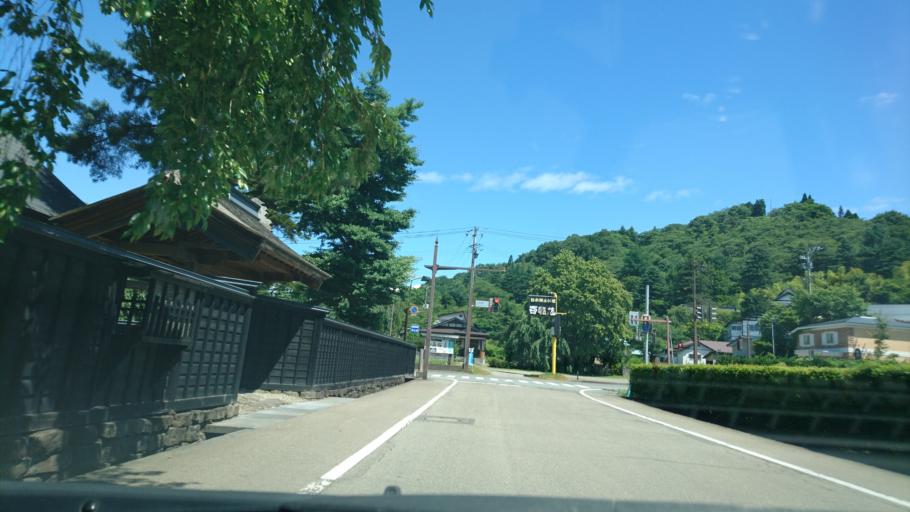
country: JP
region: Akita
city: Kakunodatemachi
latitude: 39.6022
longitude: 140.5612
